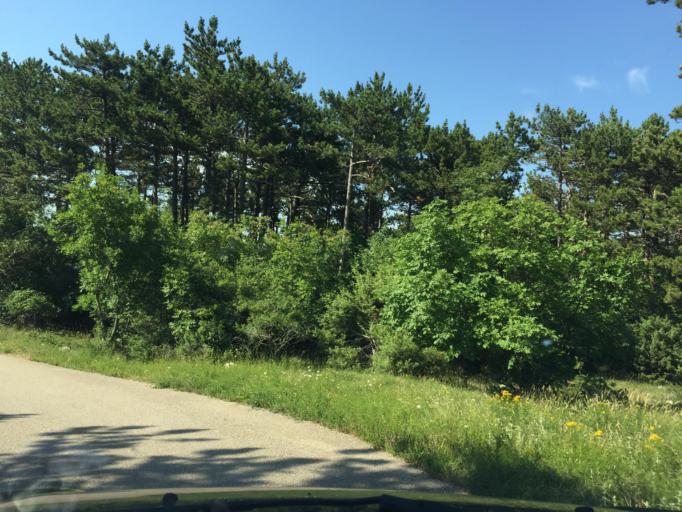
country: HR
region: Primorsko-Goranska
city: Punat
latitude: 45.0225
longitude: 14.6740
